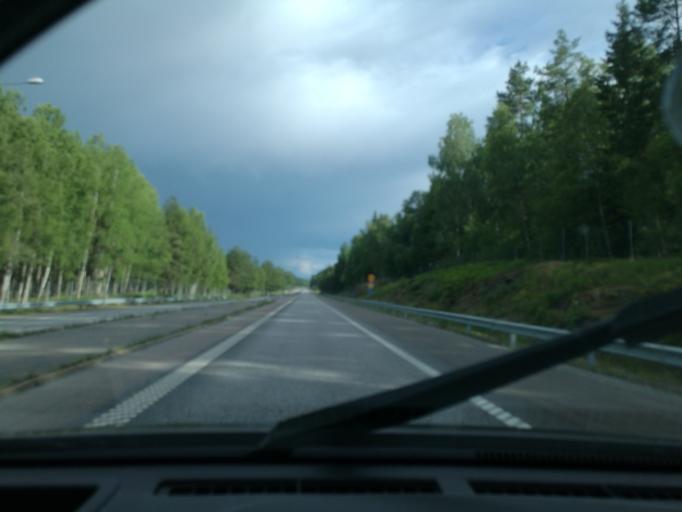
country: SE
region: Vaestmanland
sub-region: Surahammars Kommun
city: Surahammar
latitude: 59.7230
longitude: 16.2356
